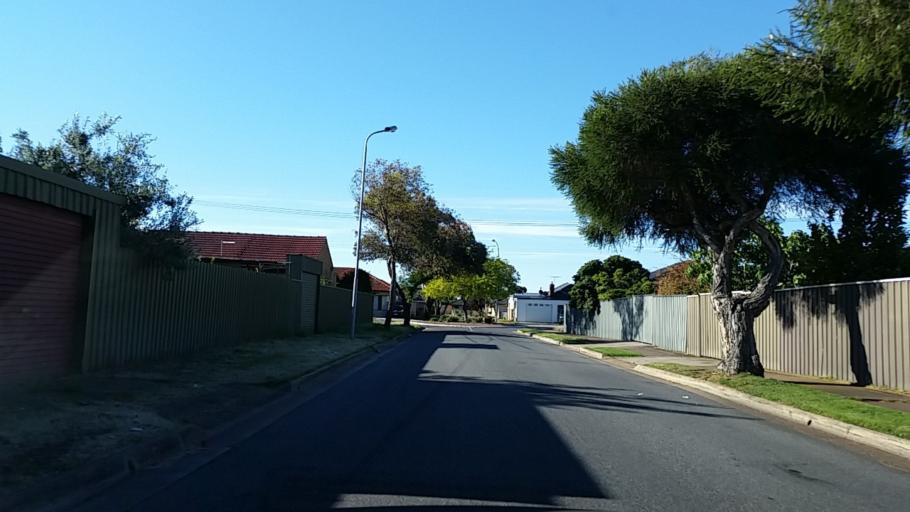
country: AU
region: South Australia
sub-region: Charles Sturt
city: Royal Park
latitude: -34.8833
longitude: 138.5149
